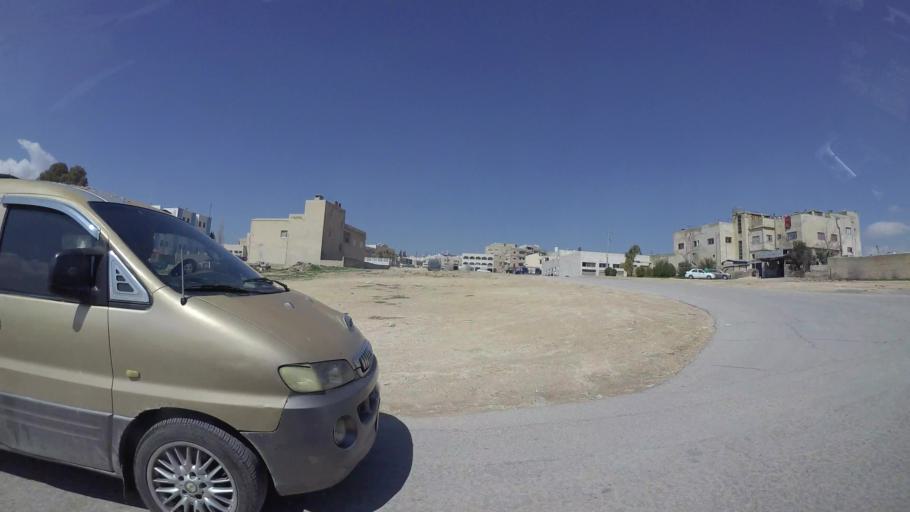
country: JO
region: Amman
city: Amman
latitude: 31.9793
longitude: 35.9994
